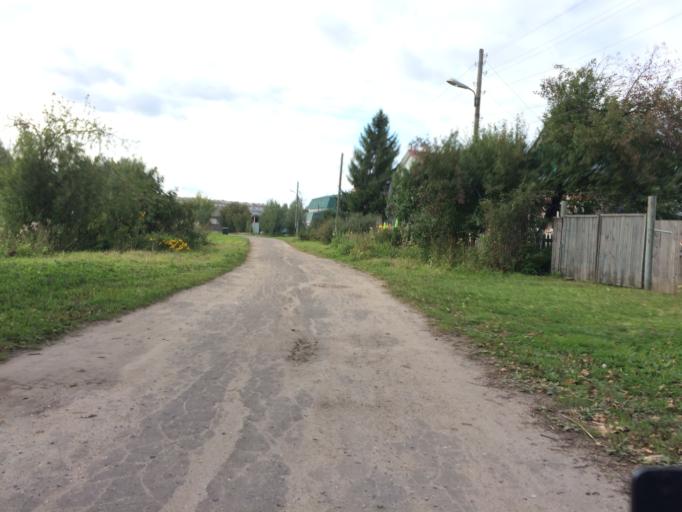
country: RU
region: Mariy-El
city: Yoshkar-Ola
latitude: 56.6531
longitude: 48.0147
